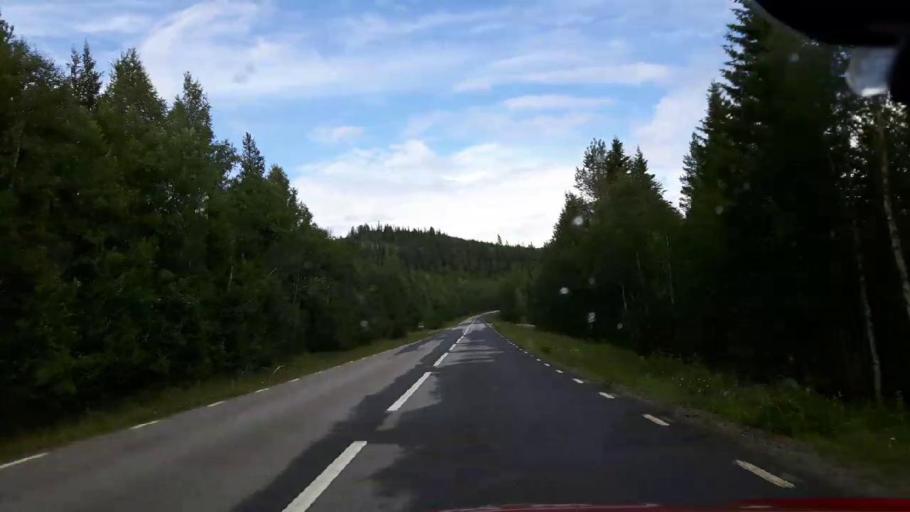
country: SE
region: Jaemtland
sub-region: Stroemsunds Kommun
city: Stroemsund
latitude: 64.3446
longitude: 15.0444
